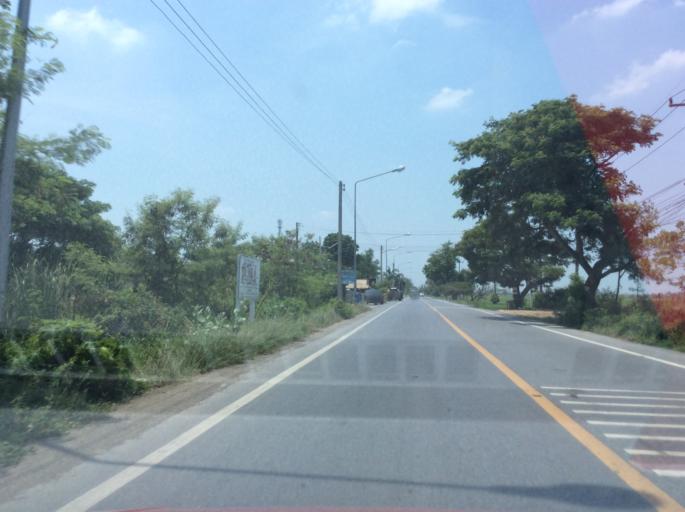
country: TH
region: Pathum Thani
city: Ban Lam Luk Ka
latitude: 13.9965
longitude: 100.7782
